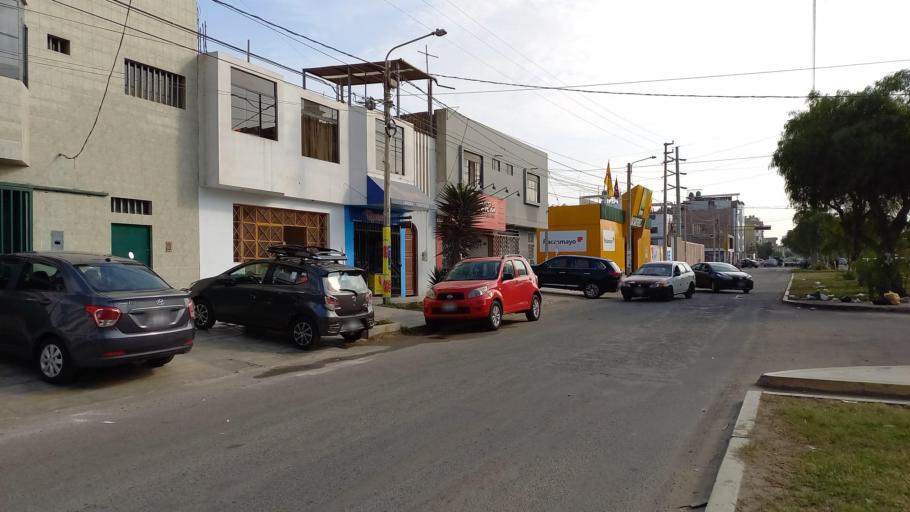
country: PE
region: La Libertad
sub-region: Provincia de Trujillo
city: Trujillo
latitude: -8.1172
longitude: -79.0448
